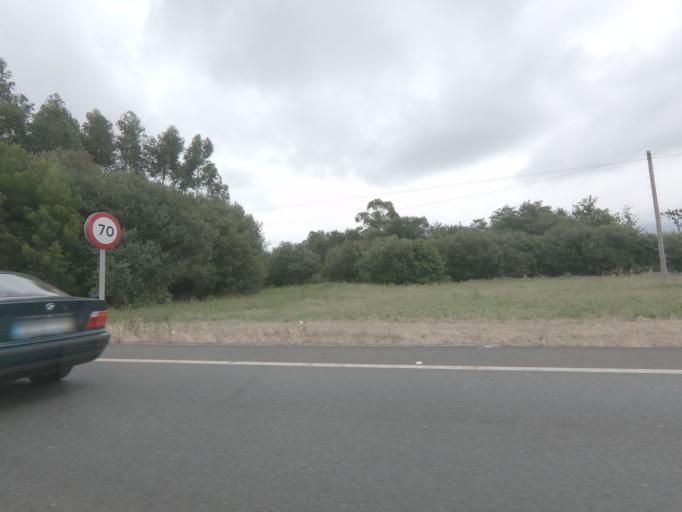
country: ES
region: Galicia
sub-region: Provincia de Pontevedra
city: Tomino
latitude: 41.9629
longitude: -8.7616
